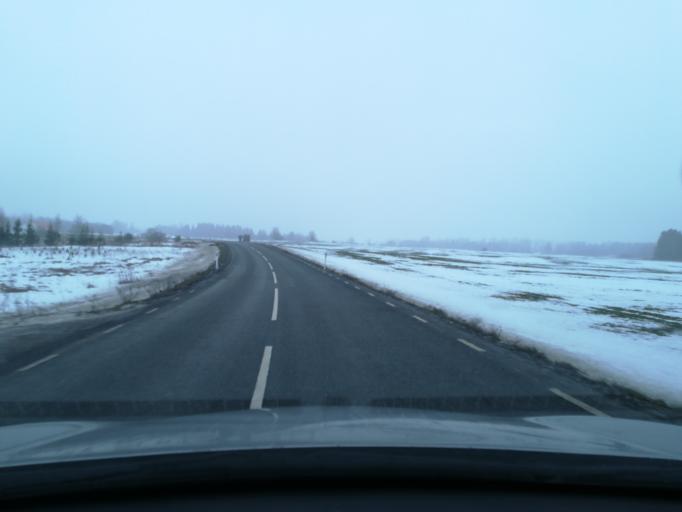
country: EE
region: Harju
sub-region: Raasiku vald
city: Raasiku
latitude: 59.3520
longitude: 25.1333
